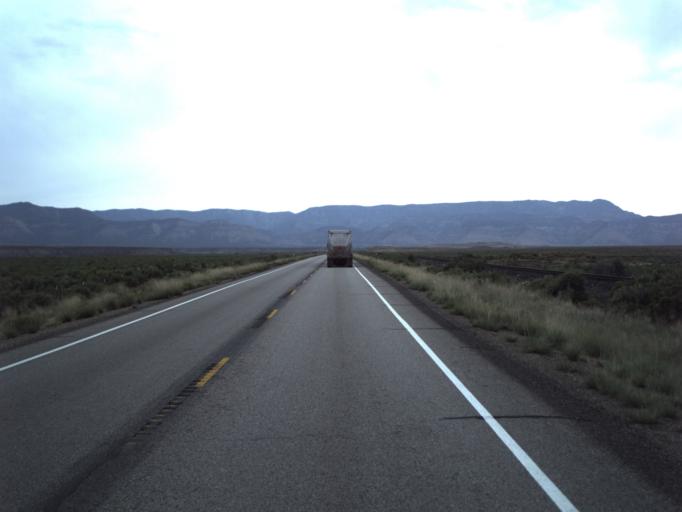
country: US
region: Utah
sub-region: Carbon County
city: East Carbon City
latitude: 39.5318
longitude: -110.5475
